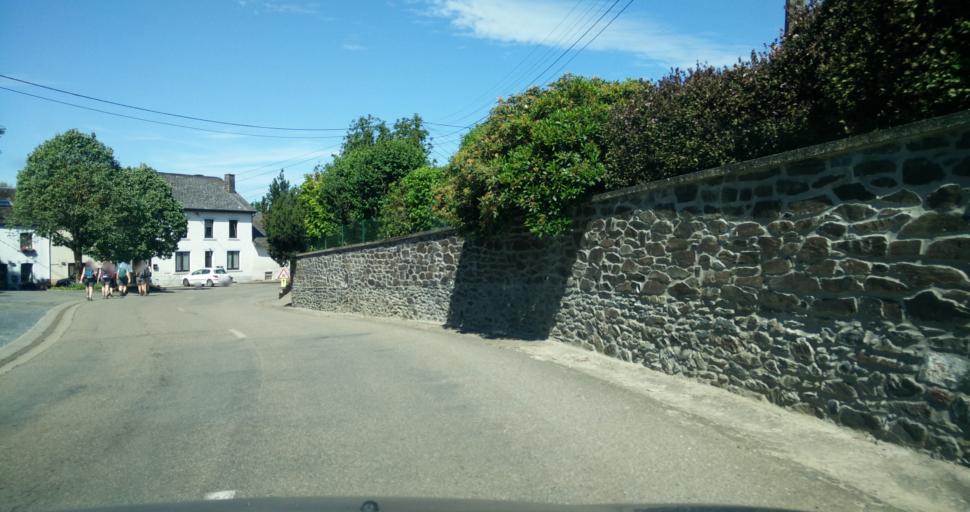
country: BE
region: Wallonia
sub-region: Province du Luxembourg
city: Houffalize
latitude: 50.1651
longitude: 5.7226
